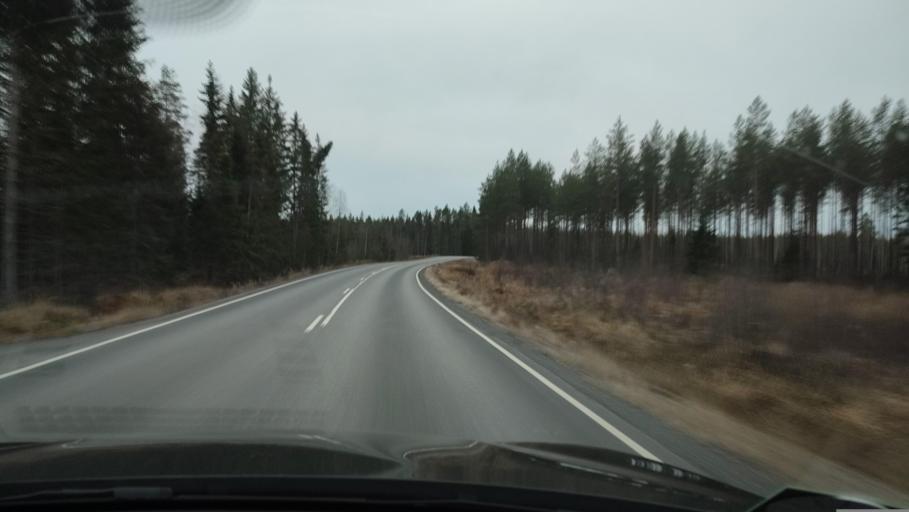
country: FI
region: Southern Ostrobothnia
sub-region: Suupohja
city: Karijoki
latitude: 62.2774
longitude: 21.5924
